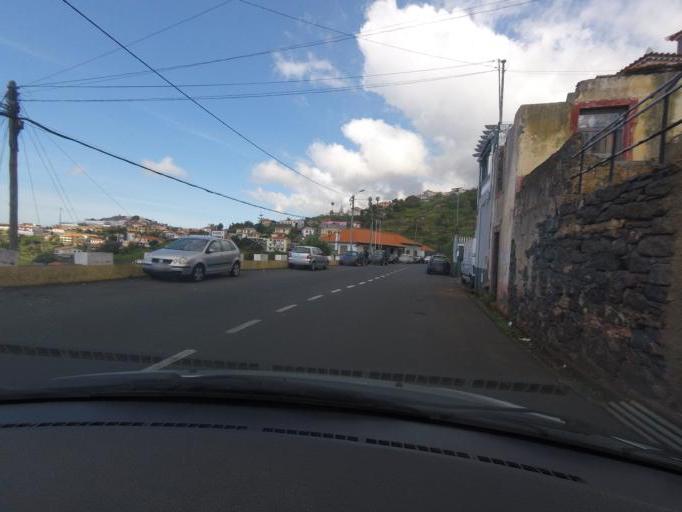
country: PT
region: Madeira
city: Camara de Lobos
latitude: 32.6701
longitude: -16.9437
